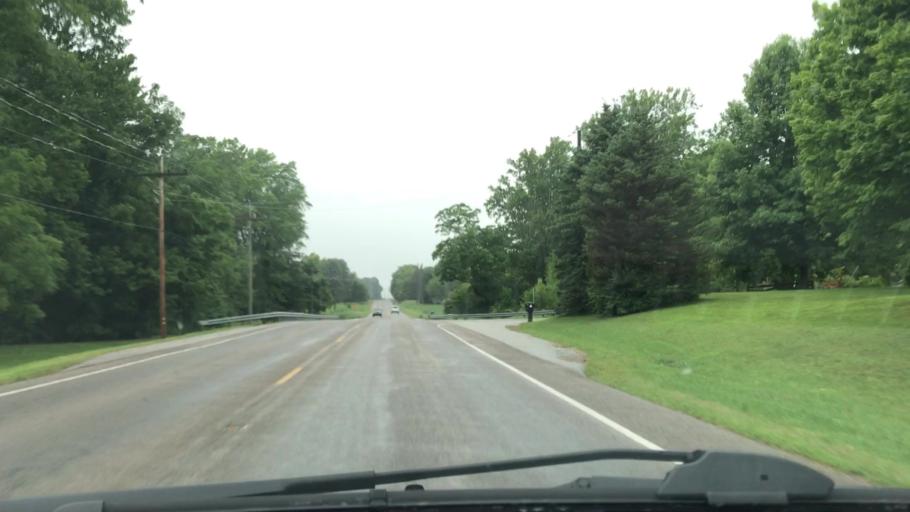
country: US
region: Indiana
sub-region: Hamilton County
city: Westfield
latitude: 40.0982
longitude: -86.1366
